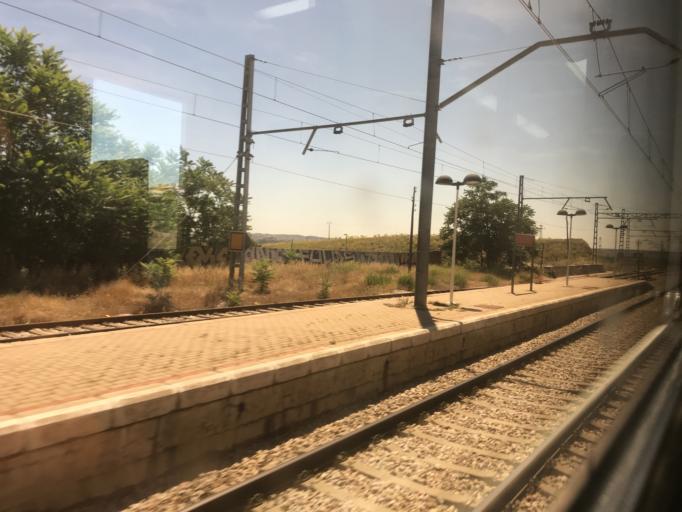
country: ES
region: Madrid
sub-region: Provincia de Madrid
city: Ciempozuelos
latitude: 40.1586
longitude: -3.6096
